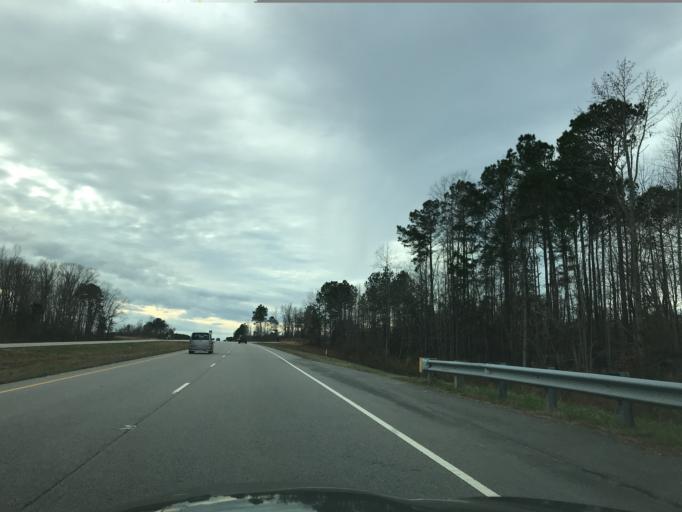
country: US
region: North Carolina
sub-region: Wake County
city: Rolesville
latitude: 35.9318
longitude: -78.4341
